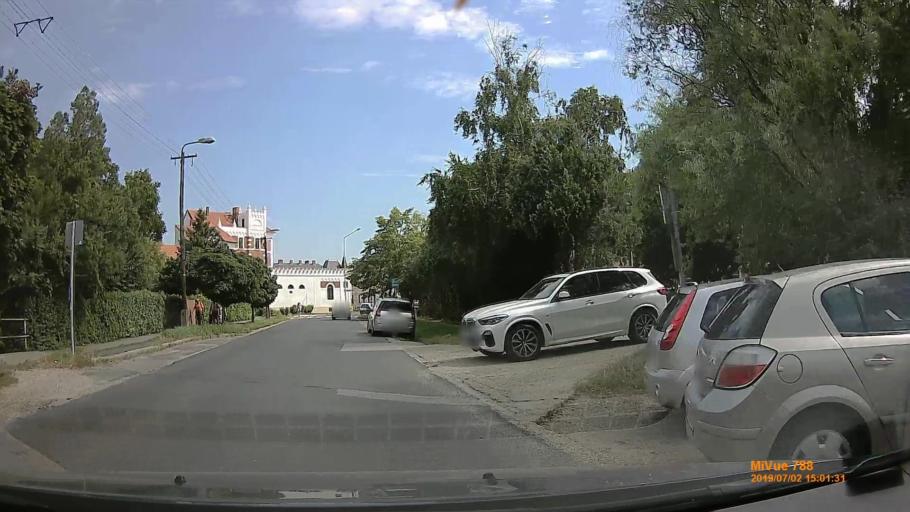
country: HU
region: Gyor-Moson-Sopron
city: Mosonmagyarovar
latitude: 47.8775
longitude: 17.2670
